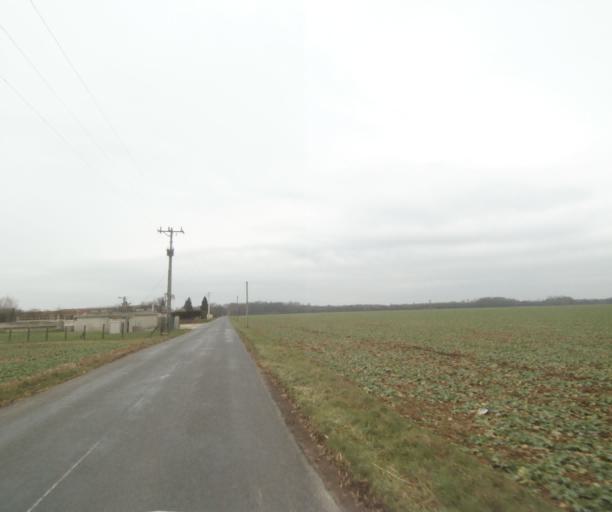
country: FR
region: Champagne-Ardenne
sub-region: Departement de la Haute-Marne
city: Villiers-en-Lieu
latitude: 48.6626
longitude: 4.8873
